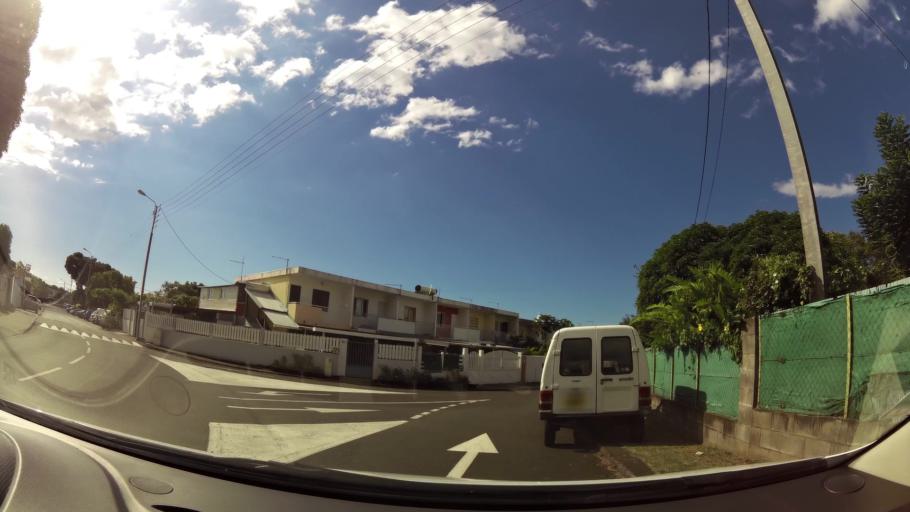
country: RE
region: Reunion
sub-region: Reunion
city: Saint-Denis
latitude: -20.8904
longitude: 55.4848
